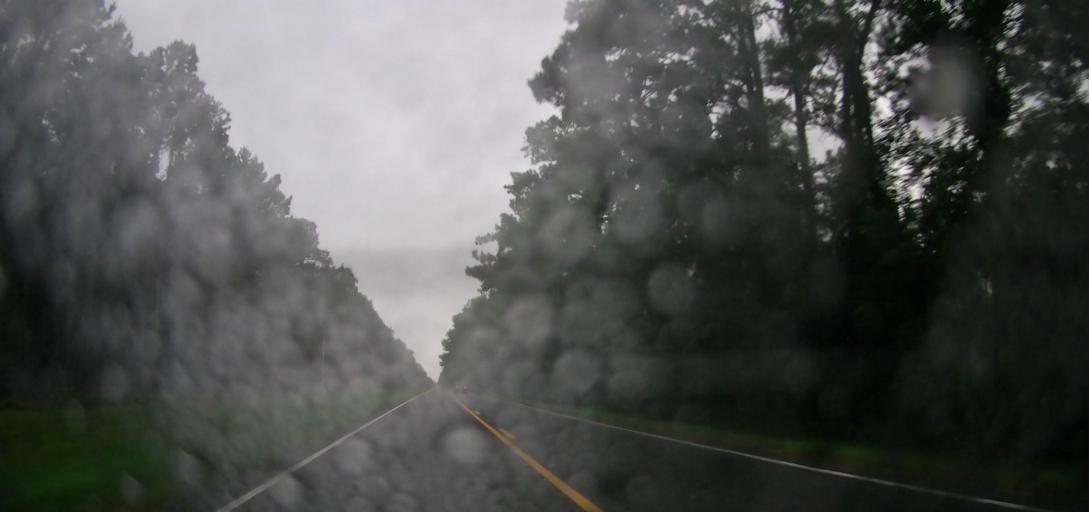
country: US
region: Georgia
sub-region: Glynn County
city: Dock Junction
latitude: 31.2582
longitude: -81.6179
